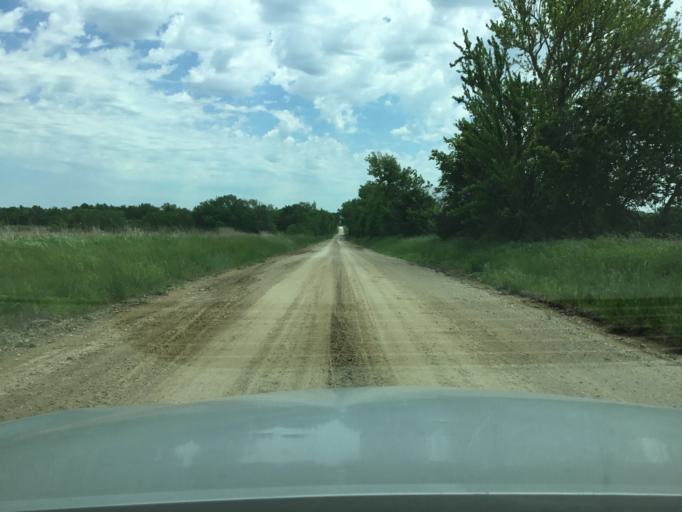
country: US
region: Kansas
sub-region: Montgomery County
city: Independence
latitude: 37.0952
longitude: -95.7964
